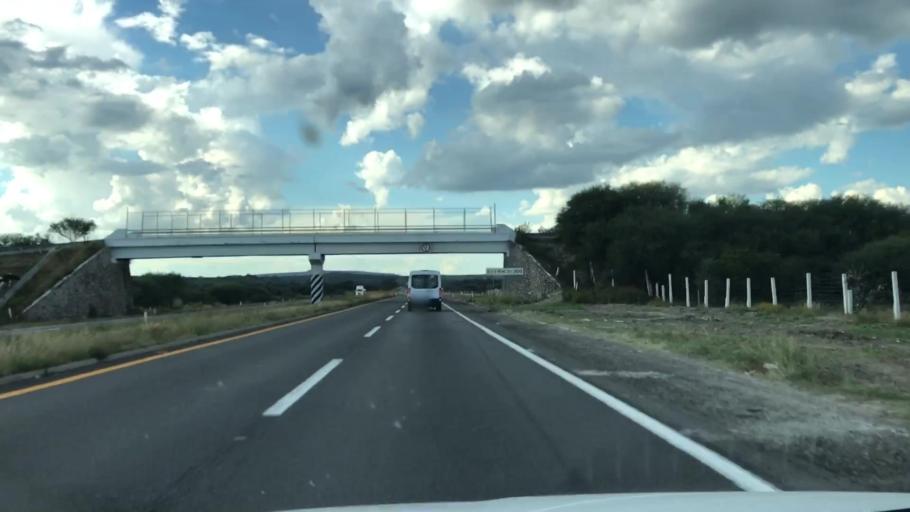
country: MX
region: Guanajuato
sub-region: Purisima del Rincon
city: Potrerillos (Guanajal)
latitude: 21.1482
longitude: -101.8425
